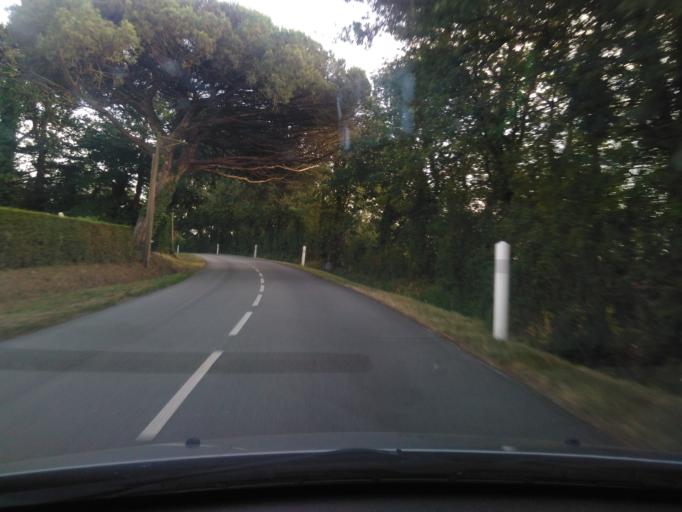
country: FR
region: Pays de la Loire
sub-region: Departement de la Vendee
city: Nesmy
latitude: 46.6140
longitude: -1.4137
